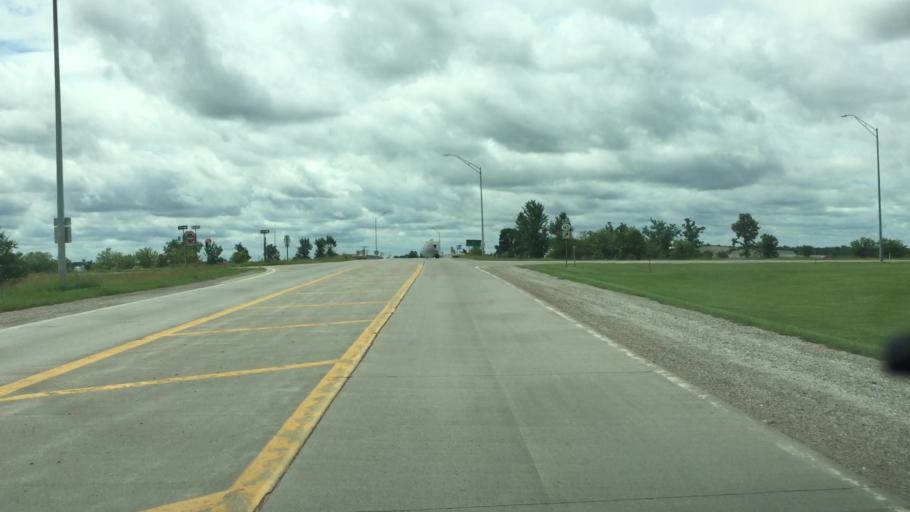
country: US
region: Iowa
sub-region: Jasper County
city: Monroe
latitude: 41.5132
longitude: -93.1014
